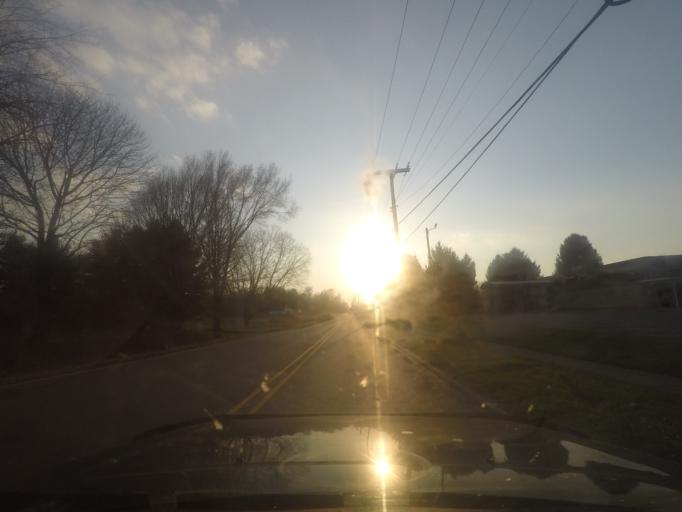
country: US
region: Indiana
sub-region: LaPorte County
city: LaPorte
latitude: 41.5915
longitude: -86.7202
